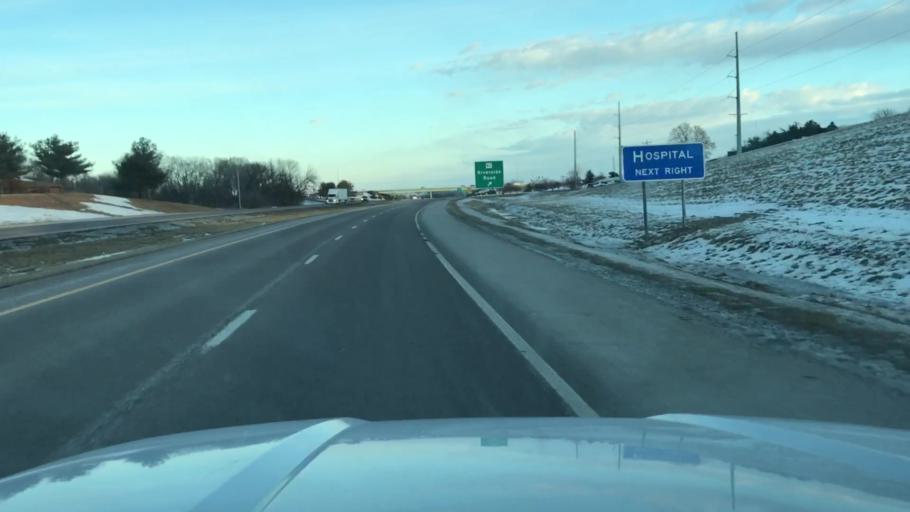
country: US
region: Missouri
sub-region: Buchanan County
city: Saint Joseph
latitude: 39.7511
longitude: -94.7749
